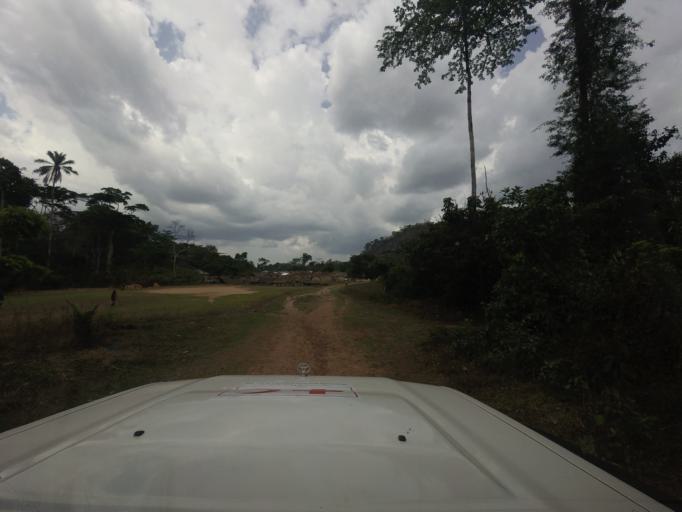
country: LR
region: Lofa
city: Voinjama
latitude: 8.3949
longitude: -9.5961
